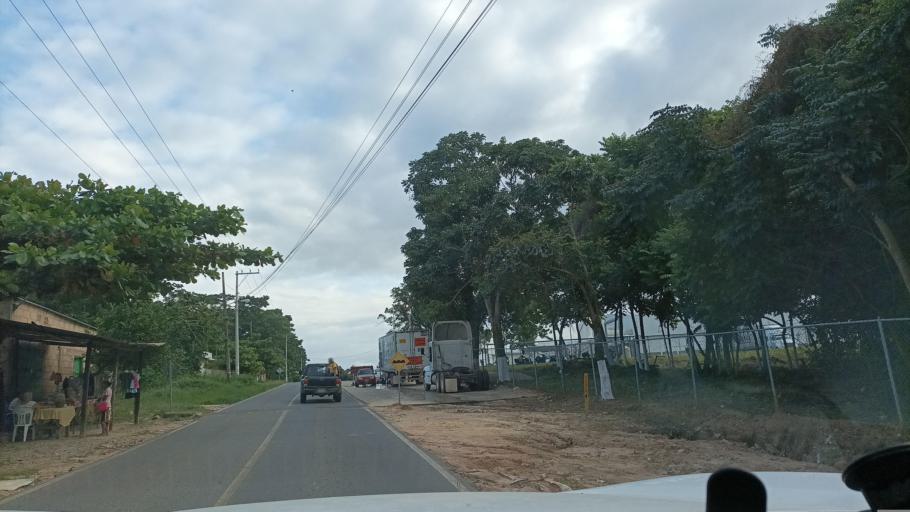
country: MX
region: Veracruz
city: Oluta
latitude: 17.9225
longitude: -94.8883
